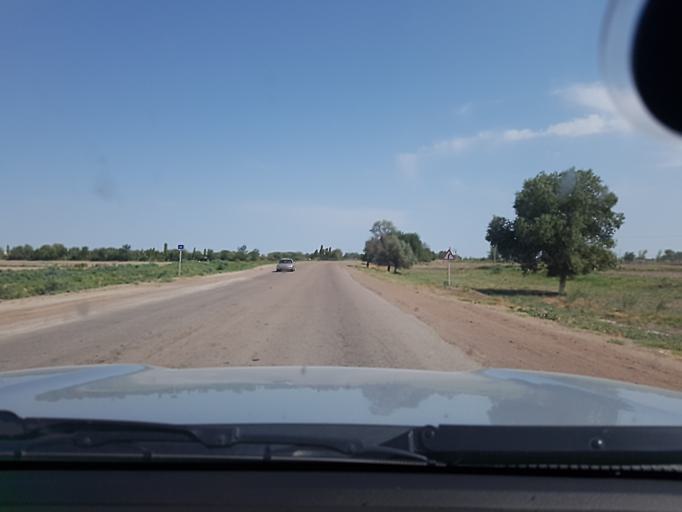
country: TM
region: Dasoguz
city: Boldumsaz
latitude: 42.2046
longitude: 59.5299
